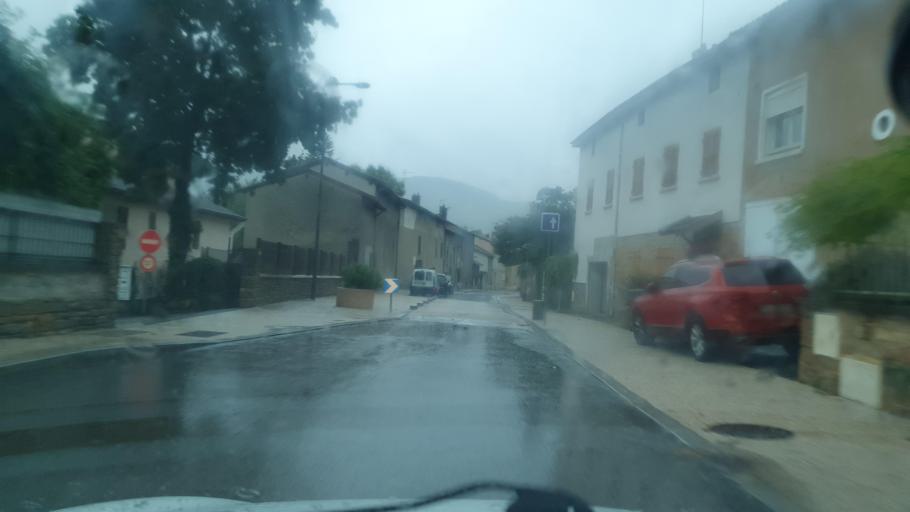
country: FR
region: Rhone-Alpes
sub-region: Departement du Rhone
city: Fontaines-sur-Saone
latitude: 45.8381
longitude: 4.8374
